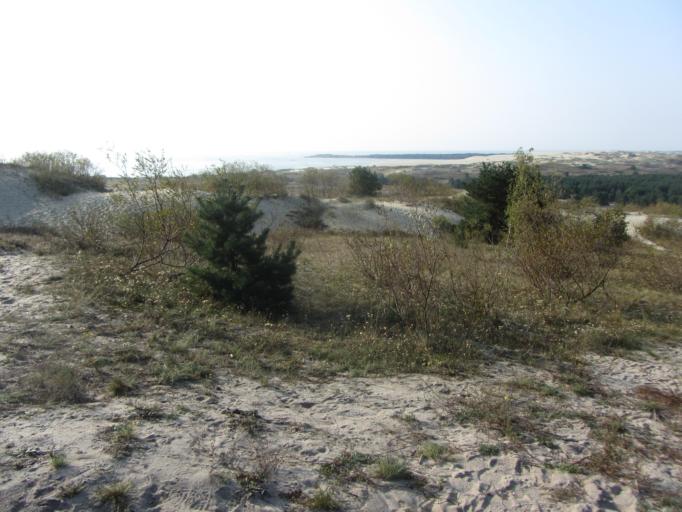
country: LT
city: Nida
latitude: 55.2951
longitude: 20.9892
